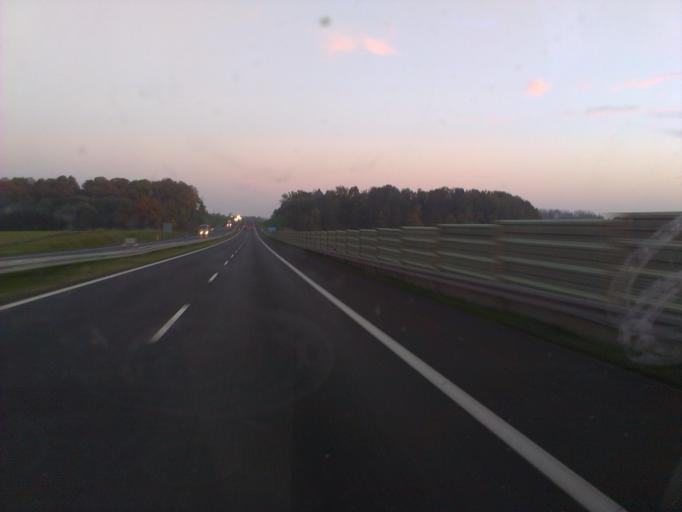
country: PL
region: Silesian Voivodeship
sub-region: Powiat gliwicki
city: Rudziniec
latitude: 50.4091
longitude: 18.4134
